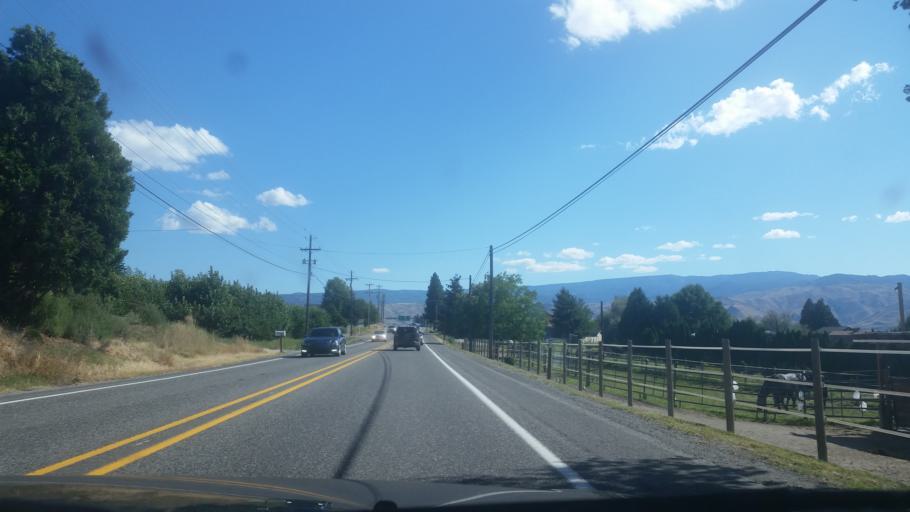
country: US
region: Washington
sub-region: Chelan County
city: Sunnyslope
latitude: 47.4751
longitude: -120.3004
